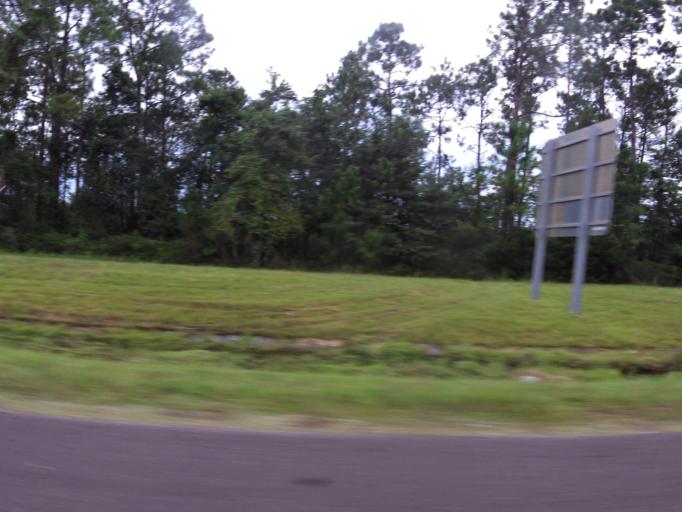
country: US
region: Florida
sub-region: Duval County
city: Baldwin
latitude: 30.3084
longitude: -81.8608
